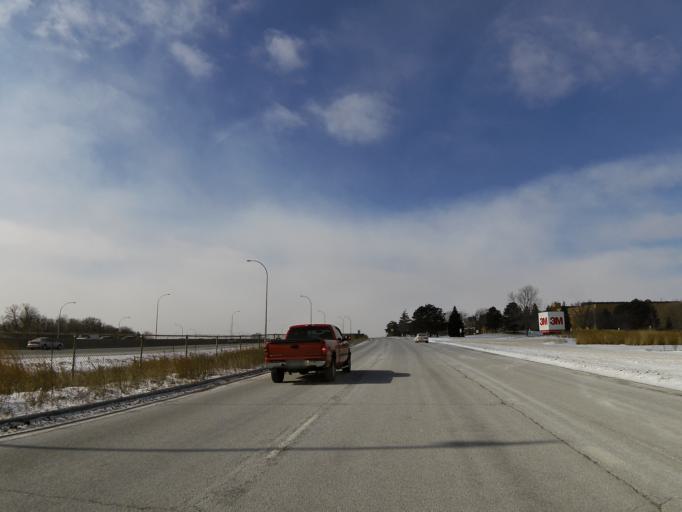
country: US
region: Minnesota
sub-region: Ramsey County
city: Maplewood
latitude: 44.9496
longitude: -92.9966
